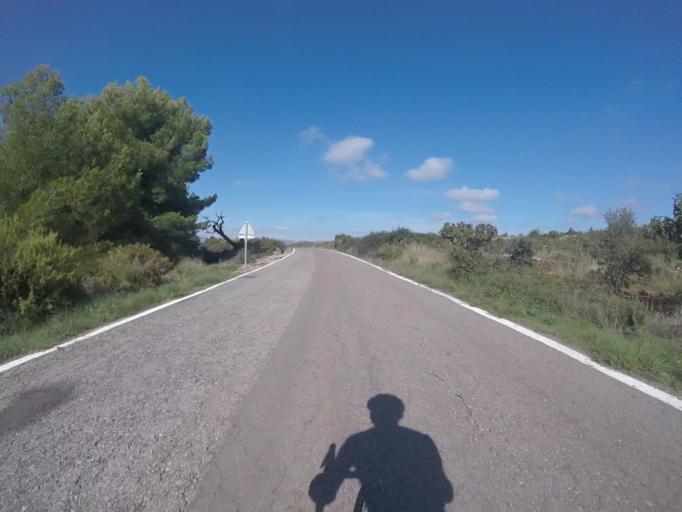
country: ES
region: Valencia
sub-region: Provincia de Castello
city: Albocasser
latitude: 40.3439
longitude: 0.0495
